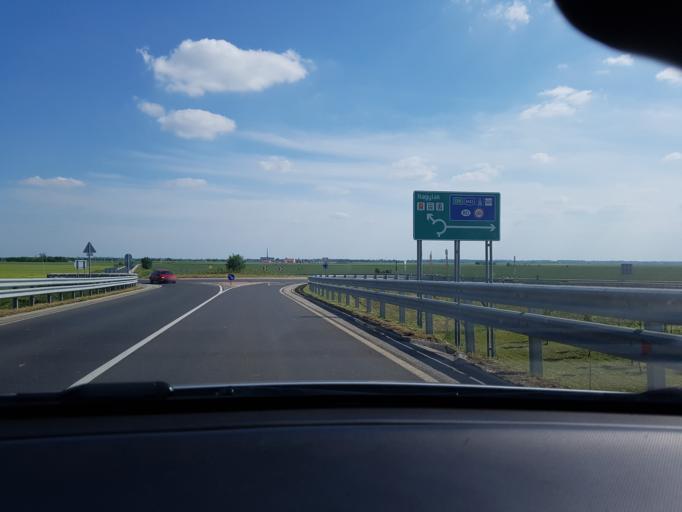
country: HU
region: Csongrad
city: Csanadpalota
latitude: 46.2152
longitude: 20.7150
